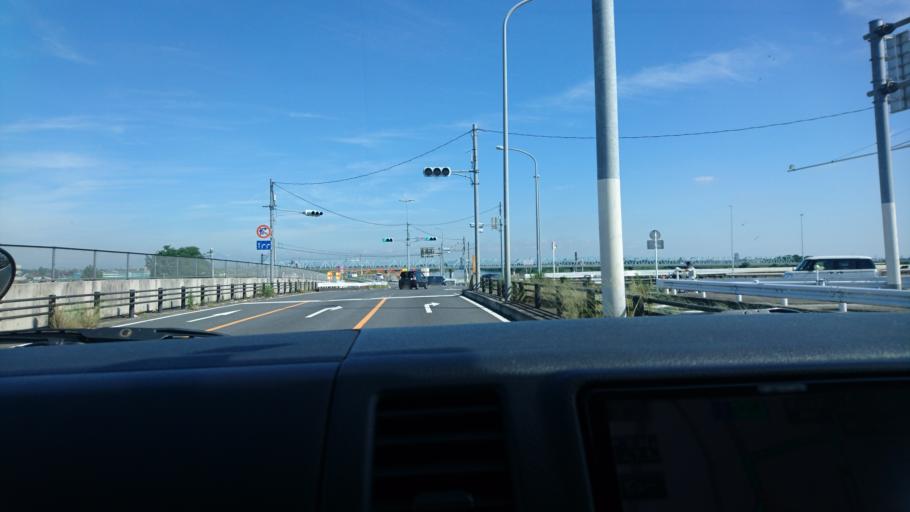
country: JP
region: Saitama
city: Kurihashi
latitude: 36.1412
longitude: 139.7035
